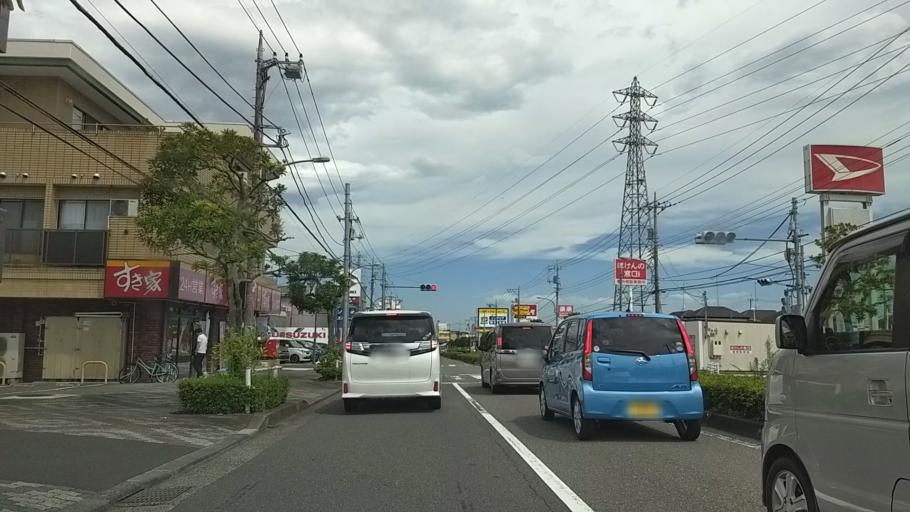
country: JP
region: Tokyo
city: Hachioji
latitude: 35.6381
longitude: 139.3033
